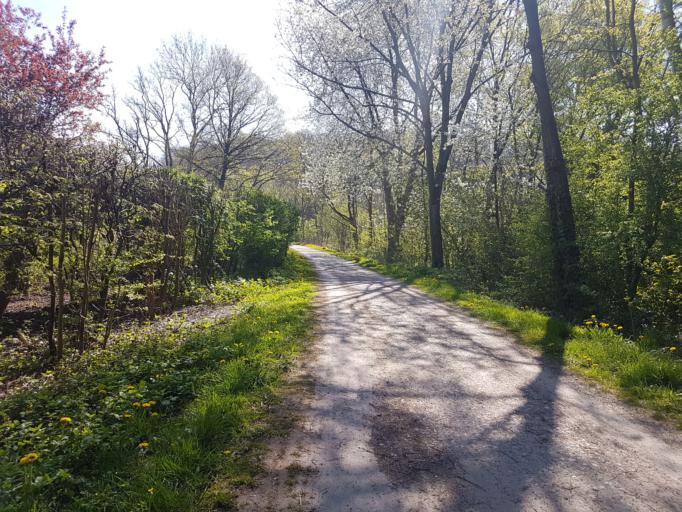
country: DE
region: North Rhine-Westphalia
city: Hattingen
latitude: 51.3729
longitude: 7.2026
